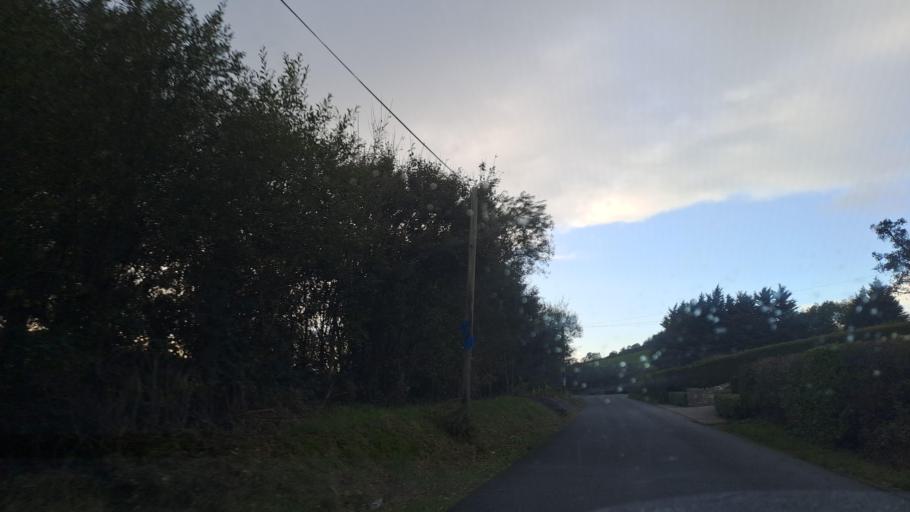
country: IE
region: Ulster
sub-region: County Monaghan
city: Castleblayney
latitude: 54.0421
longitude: -6.8351
